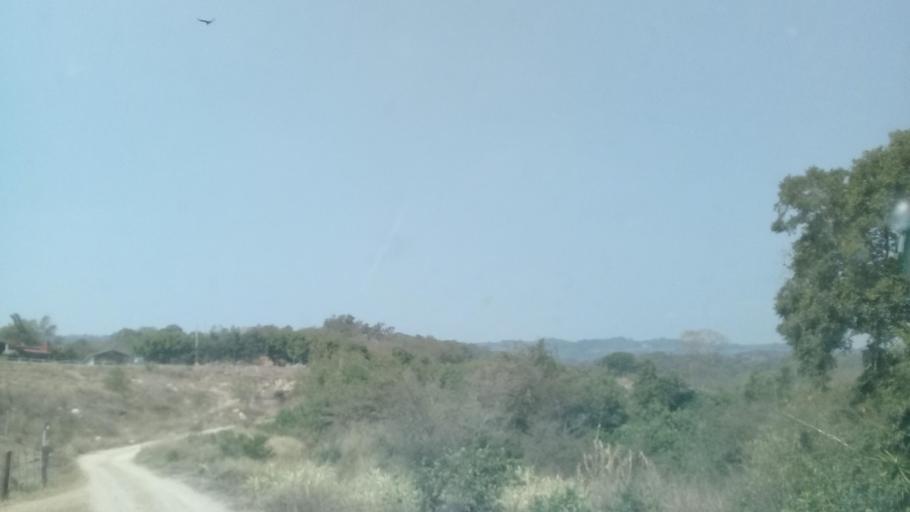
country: MX
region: Veracruz
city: El Castillo
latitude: 19.5723
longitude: -96.8028
